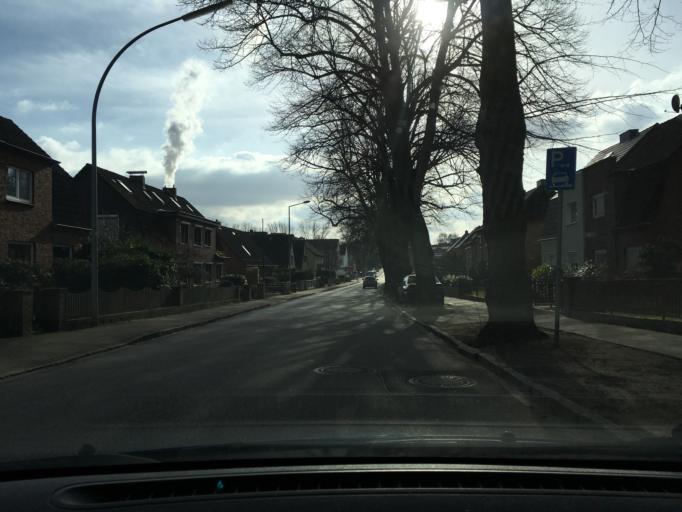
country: DE
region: Schleswig-Holstein
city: Wedel
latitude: 53.5786
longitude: 9.7225
